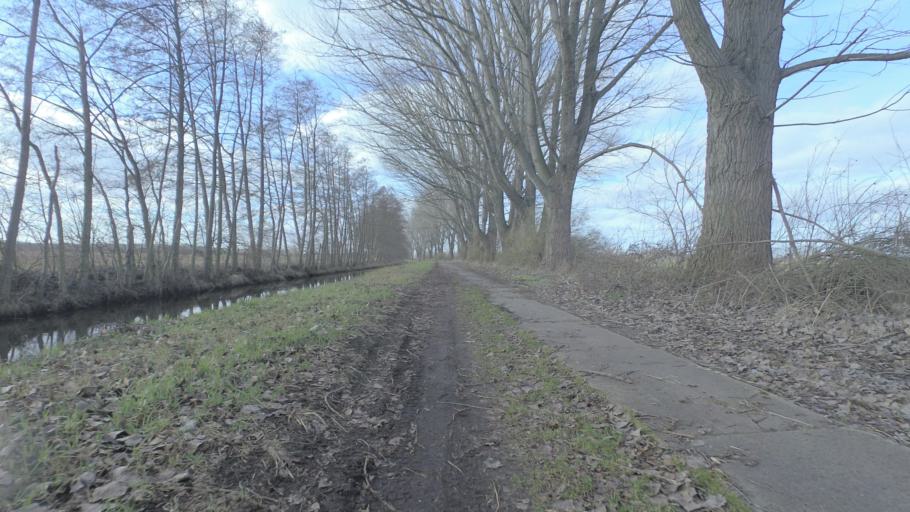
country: DE
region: Brandenburg
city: Trebbin
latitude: 52.2281
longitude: 13.2491
